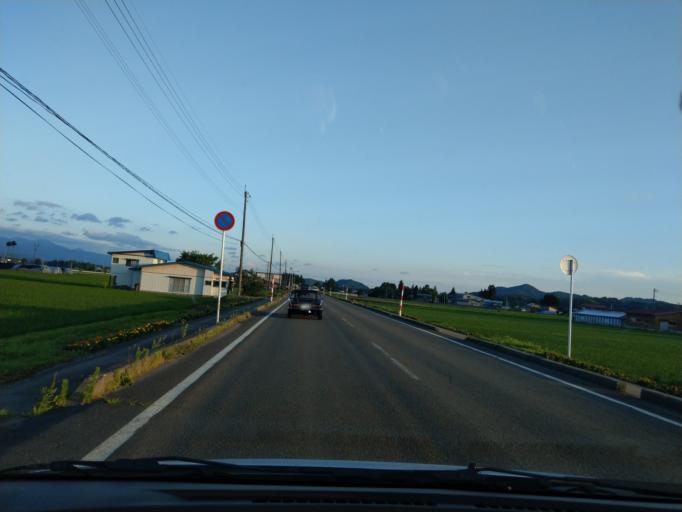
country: JP
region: Akita
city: Kakunodatemachi
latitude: 39.6488
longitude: 140.5706
